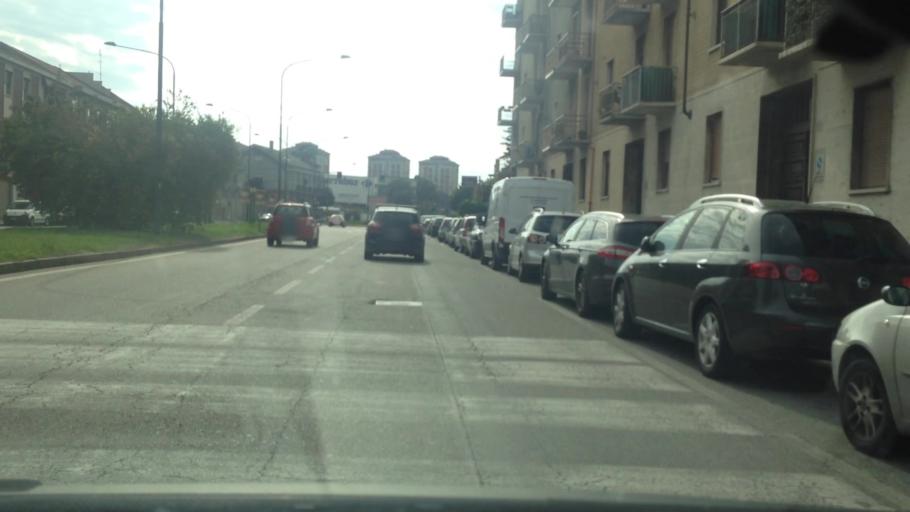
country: IT
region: Piedmont
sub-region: Provincia di Torino
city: Venaria Reale
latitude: 45.1095
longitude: 7.6532
